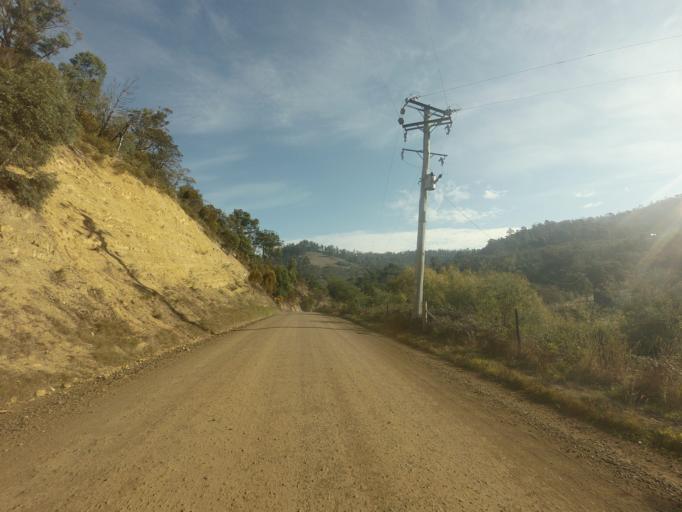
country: AU
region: Tasmania
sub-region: Sorell
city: Sorell
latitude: -42.5007
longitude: 147.4328
